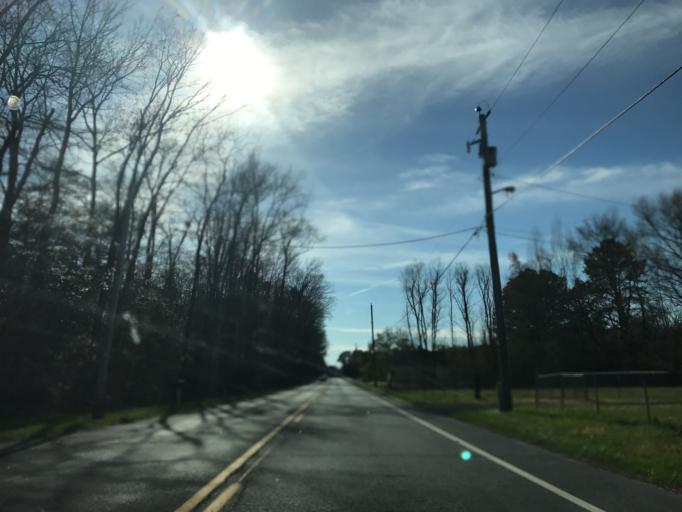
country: US
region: Maryland
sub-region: Caroline County
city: Greensboro
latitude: 39.0293
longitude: -75.7427
